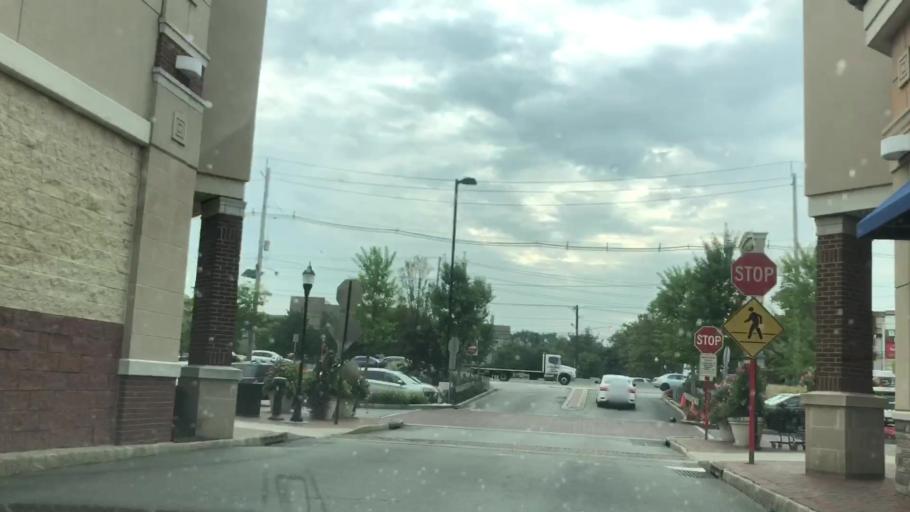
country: US
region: New Jersey
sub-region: Bergen County
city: Lyndhurst
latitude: 40.8301
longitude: -74.1372
